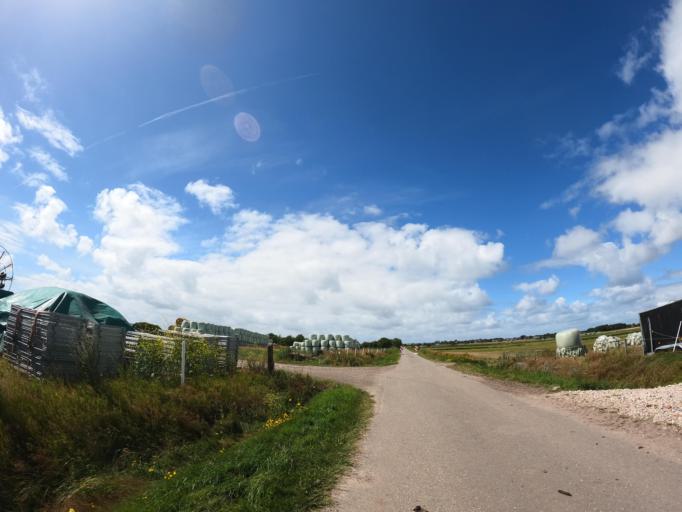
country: DE
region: Schleswig-Holstein
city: Tinnum
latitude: 54.8886
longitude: 8.3465
